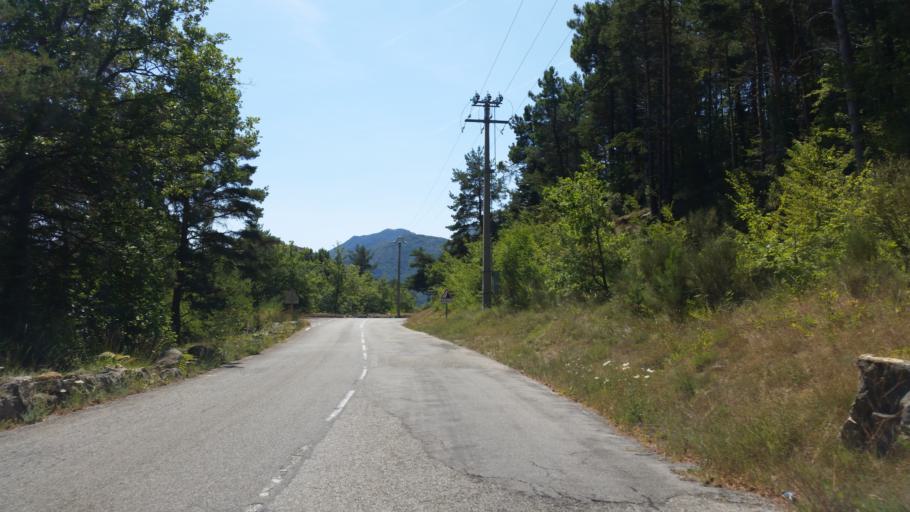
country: FR
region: Provence-Alpes-Cote d'Azur
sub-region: Departement des Alpes-Maritimes
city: Breil-sur-Roya
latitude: 43.9135
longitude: 7.4825
